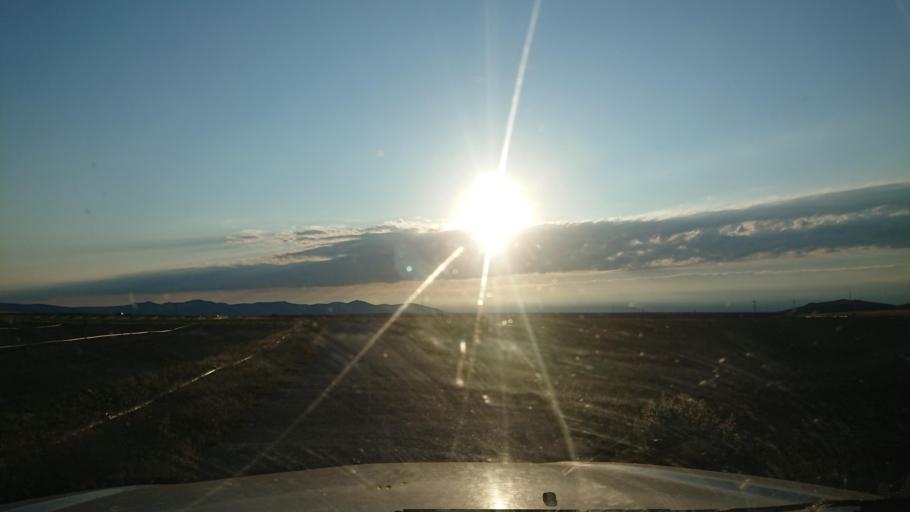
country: TR
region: Aksaray
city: Sariyahsi
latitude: 39.0199
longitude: 33.8879
